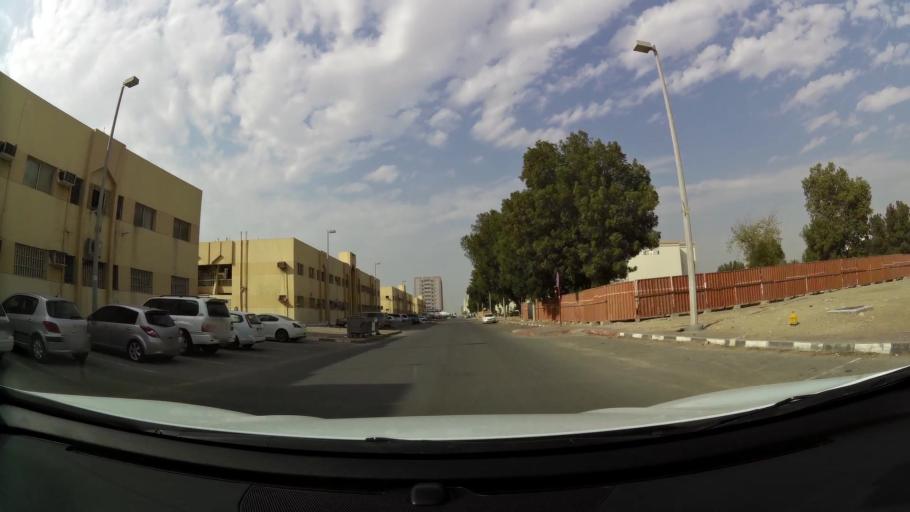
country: AE
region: Abu Dhabi
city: Abu Dhabi
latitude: 24.3183
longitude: 54.5311
